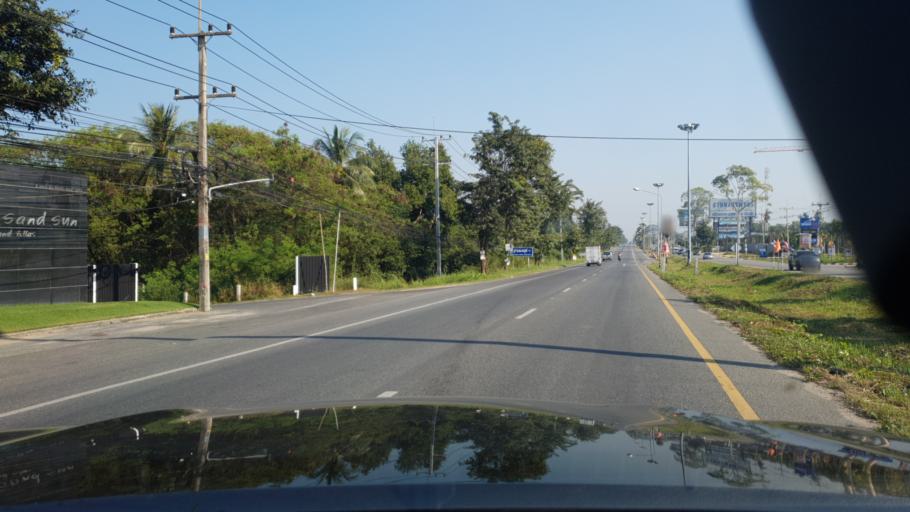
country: TH
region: Chon Buri
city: Sattahip
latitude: 12.7762
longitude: 100.9112
